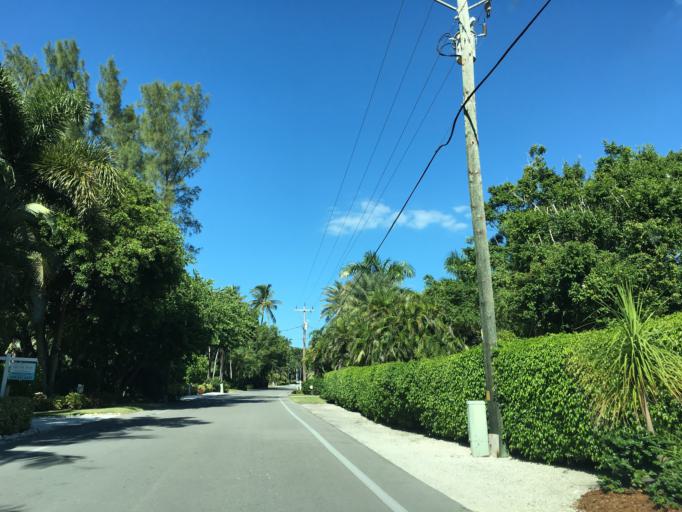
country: US
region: Florida
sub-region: Lee County
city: Pine Island Center
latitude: 26.5445
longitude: -82.1970
